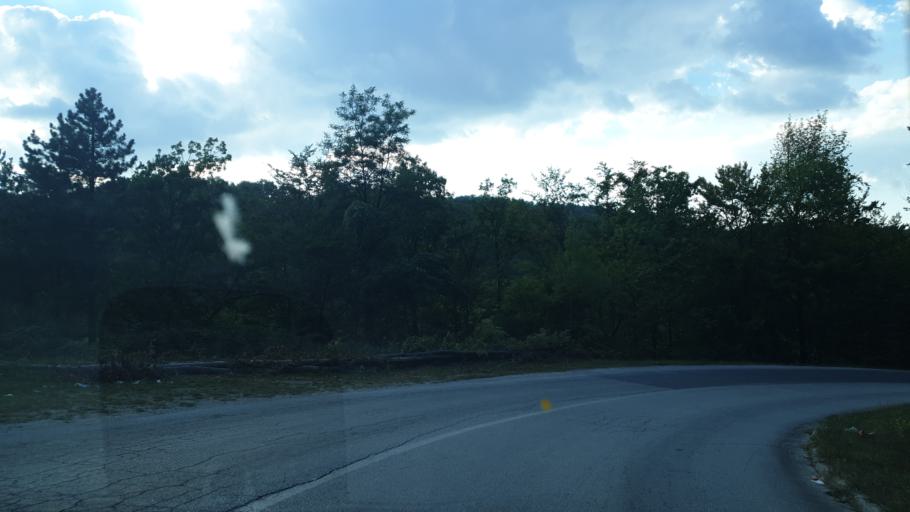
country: RS
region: Central Serbia
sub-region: Zlatiborski Okrug
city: Uzice
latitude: 43.8653
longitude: 19.9065
